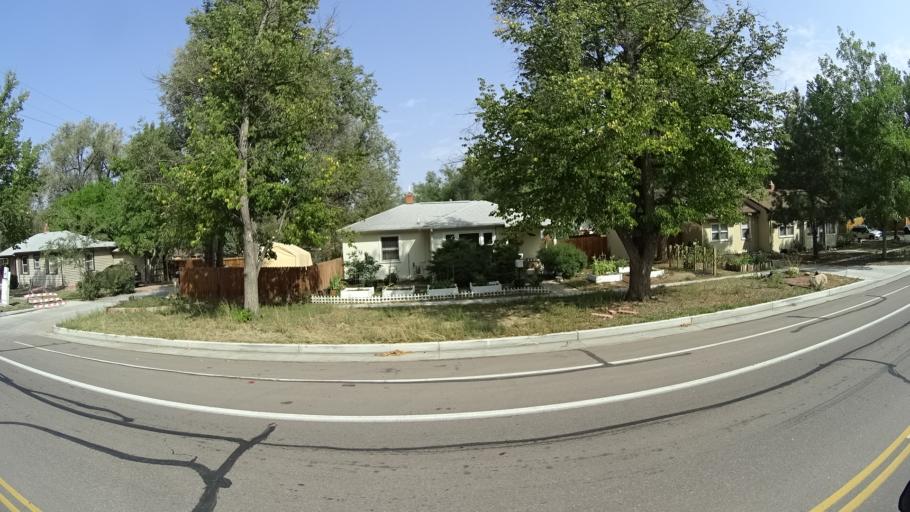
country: US
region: Colorado
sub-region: El Paso County
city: Colorado Springs
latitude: 38.8360
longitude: -104.8013
